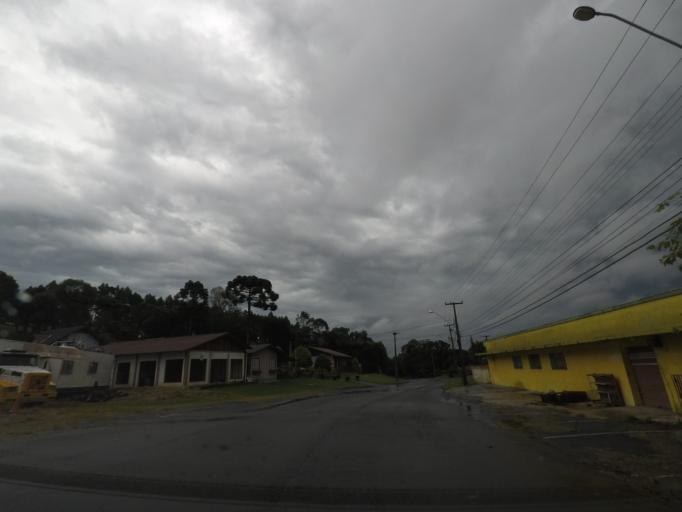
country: BR
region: Parana
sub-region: Campo Largo
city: Campo Largo
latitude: -25.4474
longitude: -49.4555
